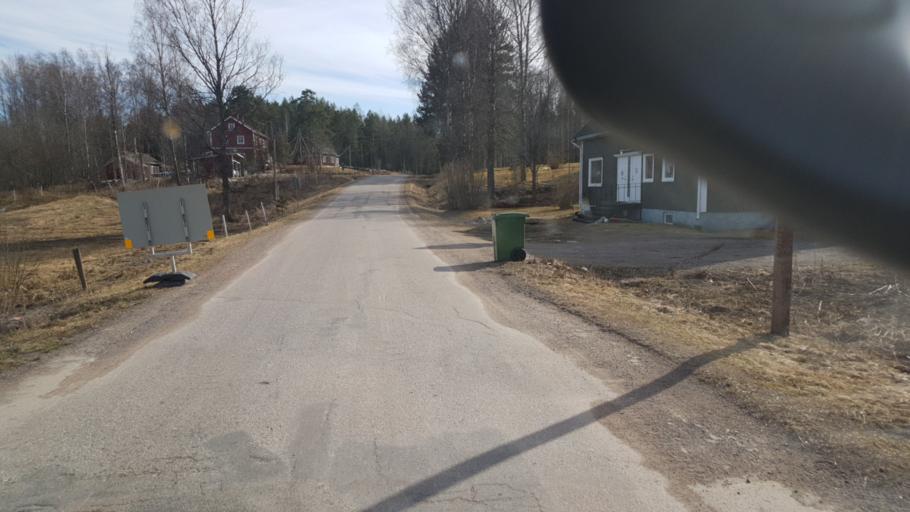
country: SE
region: Vaermland
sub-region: Eda Kommun
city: Charlottenberg
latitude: 59.8572
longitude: 12.3431
